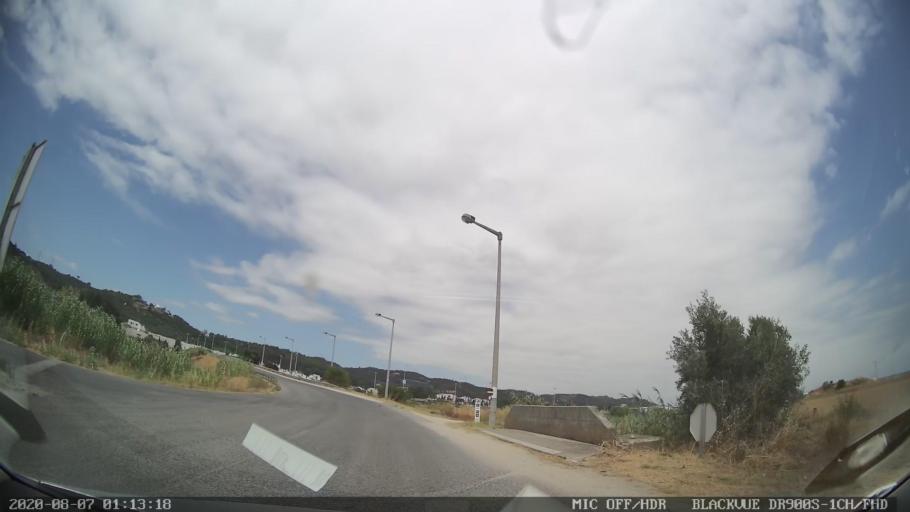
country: PT
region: Lisbon
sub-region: Vila Franca de Xira
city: Vila Franca de Xira
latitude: 38.9668
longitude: -8.9786
